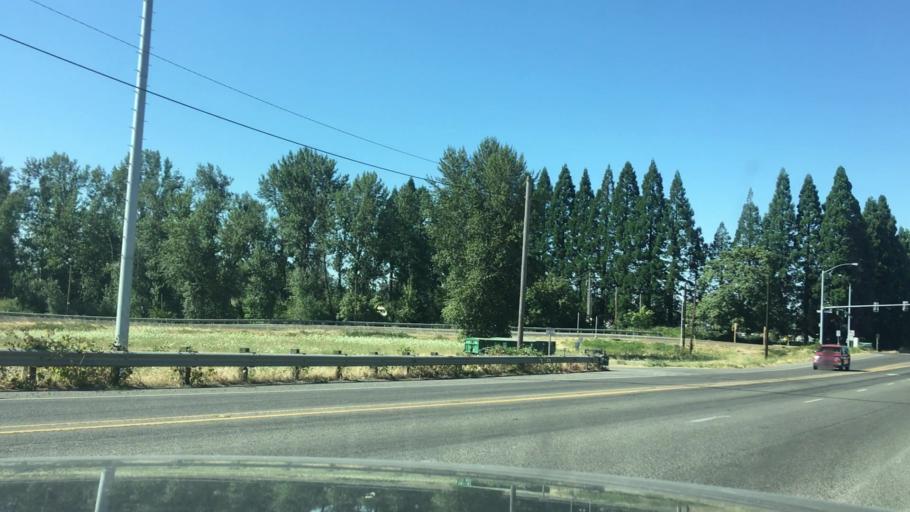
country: US
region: Oregon
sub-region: Lane County
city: Eugene
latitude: 44.0930
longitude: -123.0986
